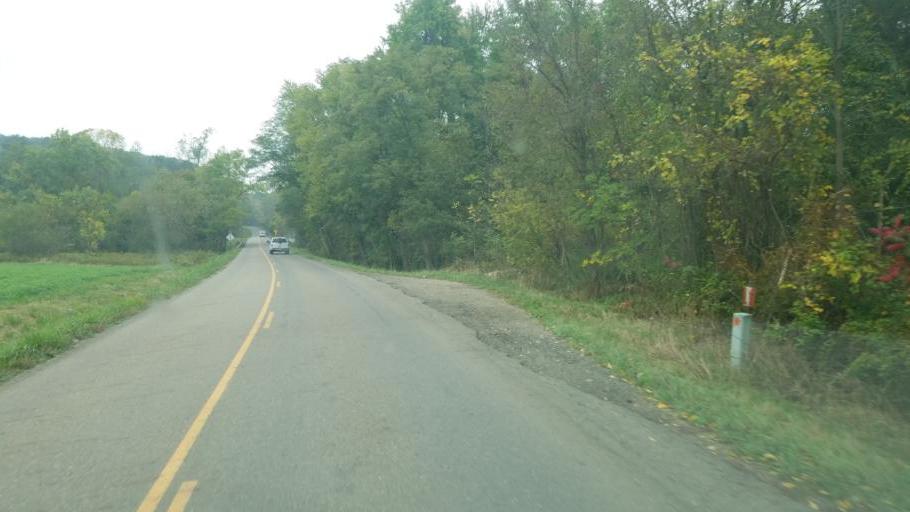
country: US
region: Ohio
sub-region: Tuscarawas County
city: Strasburg
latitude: 40.6348
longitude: -81.3960
